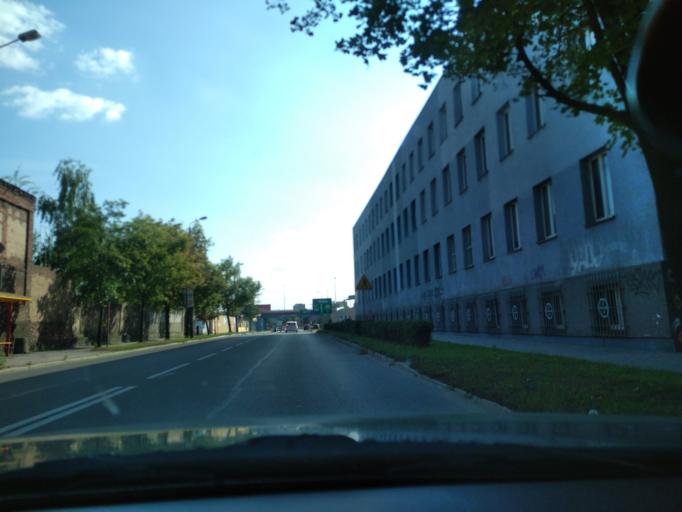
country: PL
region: Silesian Voivodeship
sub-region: Gliwice
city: Gliwice
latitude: 50.3064
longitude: 18.6624
